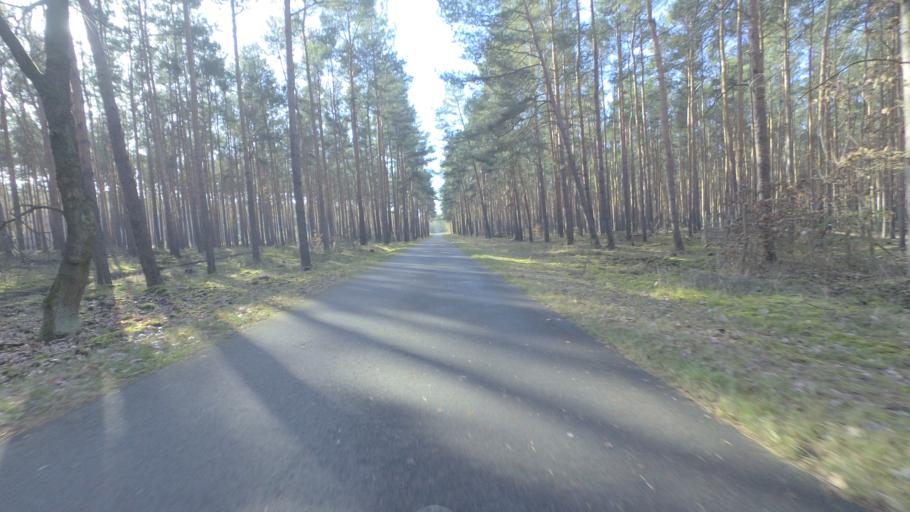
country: DE
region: Brandenburg
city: Luckenwalde
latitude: 52.0497
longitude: 13.1478
